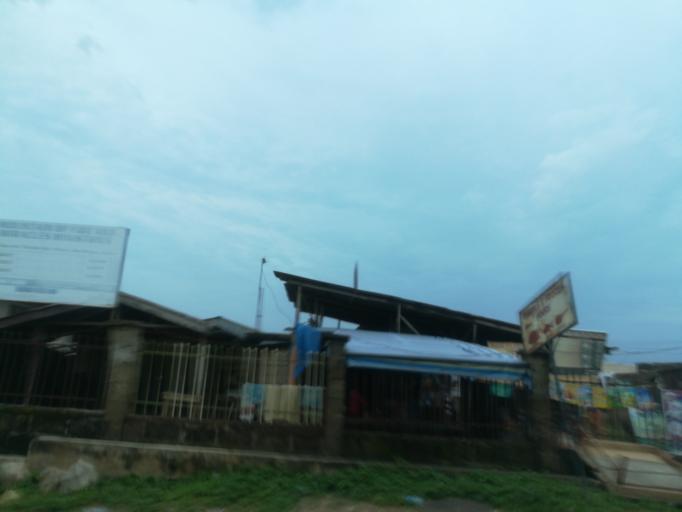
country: NG
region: Oyo
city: Moniya
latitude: 7.4545
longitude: 3.9144
